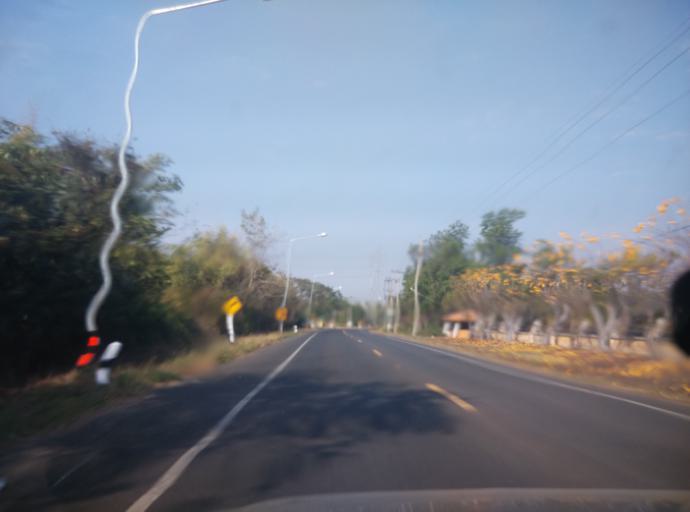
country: TH
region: Sisaket
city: Si Sa Ket
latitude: 15.1123
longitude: 104.2708
